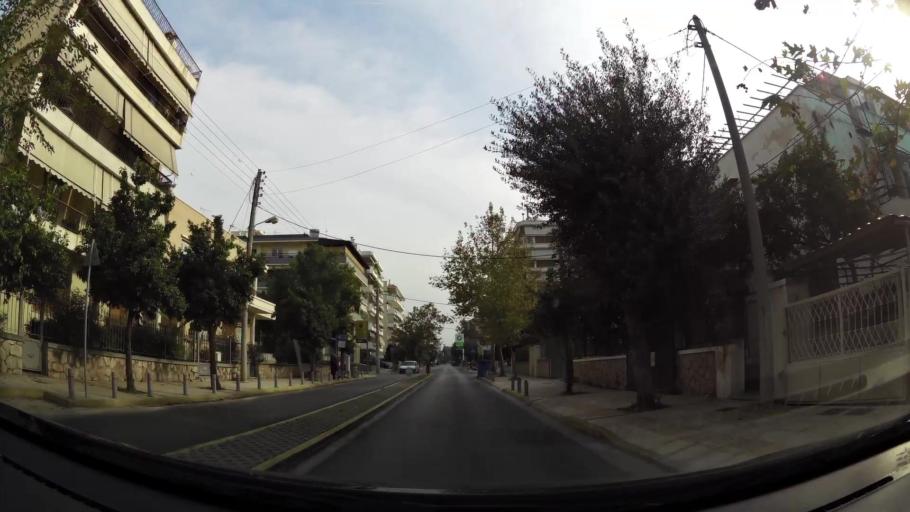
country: GR
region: Attica
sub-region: Nomarchia Athinas
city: Kallithea
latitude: 37.9581
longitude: 23.6929
